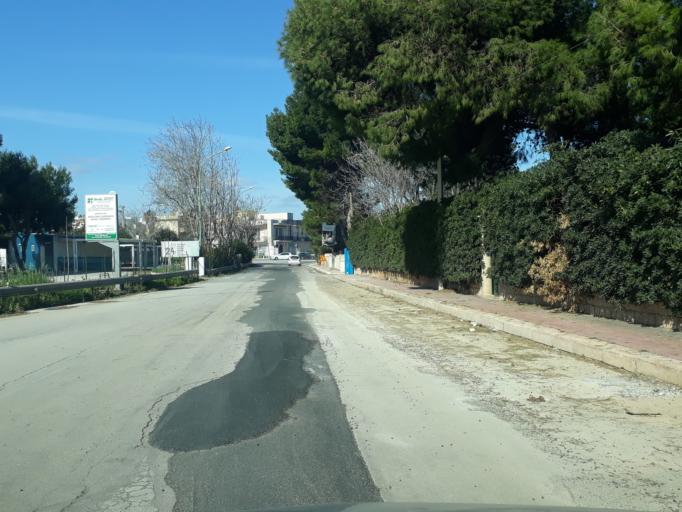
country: IT
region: Apulia
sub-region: Provincia di Brindisi
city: Fasano
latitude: 40.9049
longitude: 17.3504
